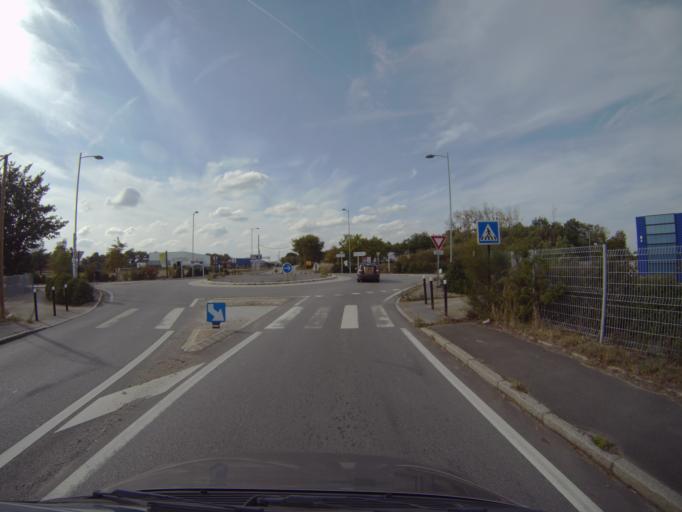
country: FR
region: Pays de la Loire
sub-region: Departement de la Loire-Atlantique
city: Sautron
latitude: 47.2432
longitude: -1.6752
